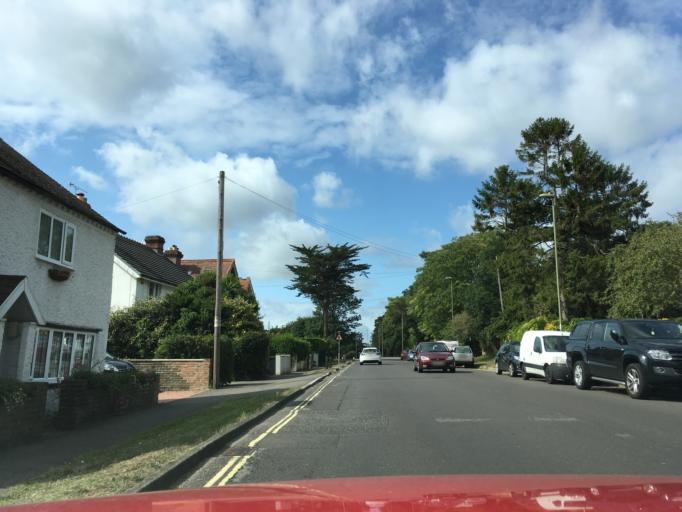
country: GB
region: England
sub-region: Hampshire
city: Havant
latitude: 50.8532
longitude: -1.0084
